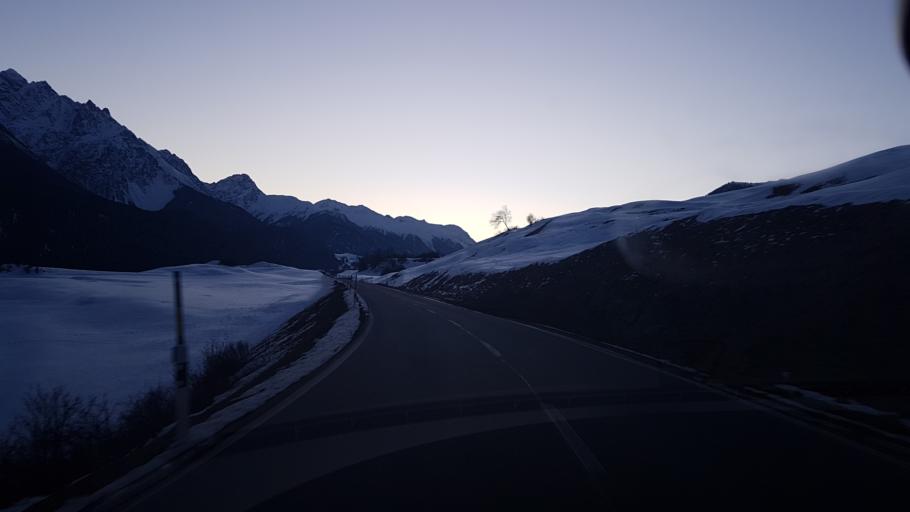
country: CH
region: Grisons
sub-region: Inn District
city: Scuol
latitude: 46.8128
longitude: 10.3443
